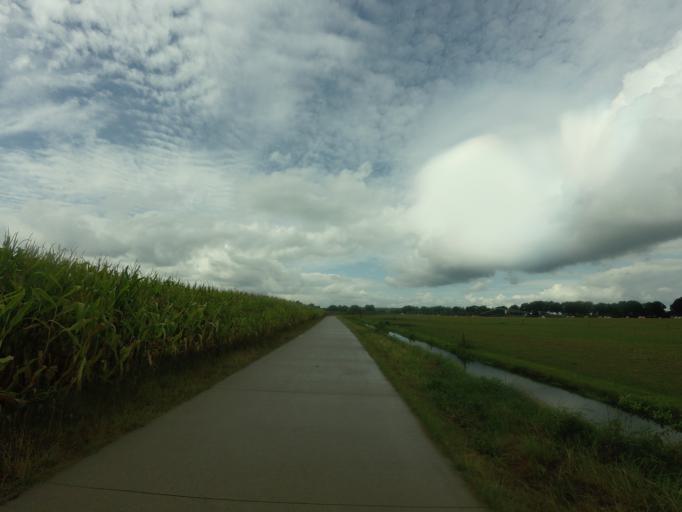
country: NL
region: Overijssel
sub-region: Gemeente Dalfsen
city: Dalfsen
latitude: 52.6104
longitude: 6.3473
